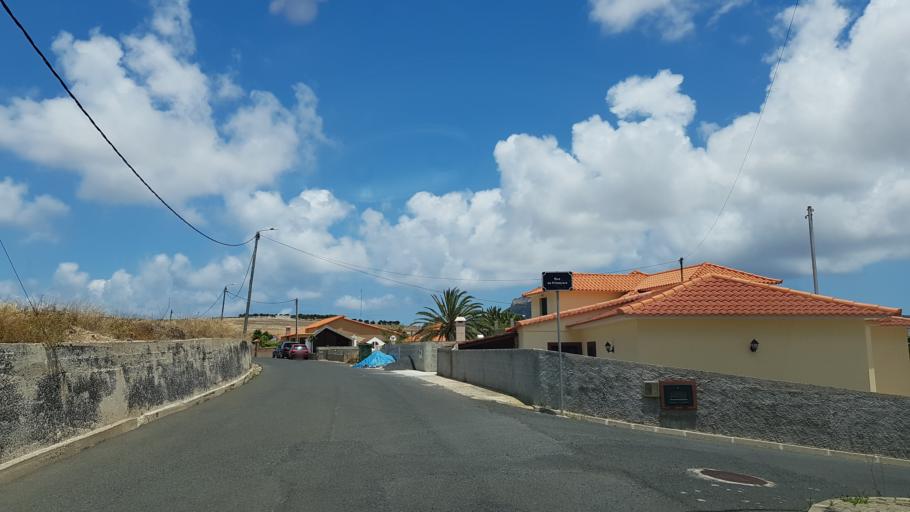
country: PT
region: Madeira
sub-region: Porto Santo
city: Vila de Porto Santo
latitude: 33.0578
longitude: -16.3601
